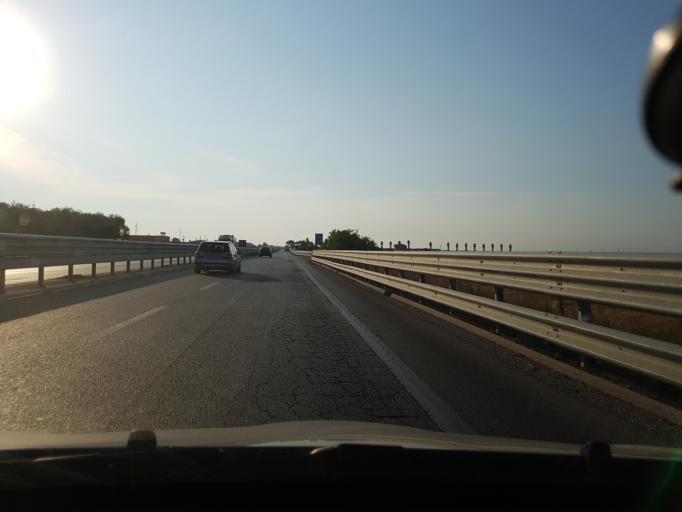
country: IT
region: Apulia
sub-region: Provincia di Foggia
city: Stornara
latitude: 41.3120
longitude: 15.7991
